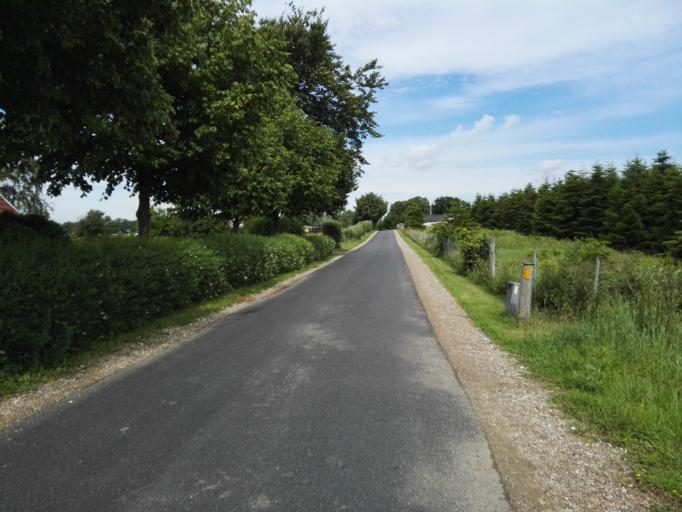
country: DK
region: Capital Region
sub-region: Egedal Kommune
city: Olstykke
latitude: 55.8141
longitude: 12.1759
